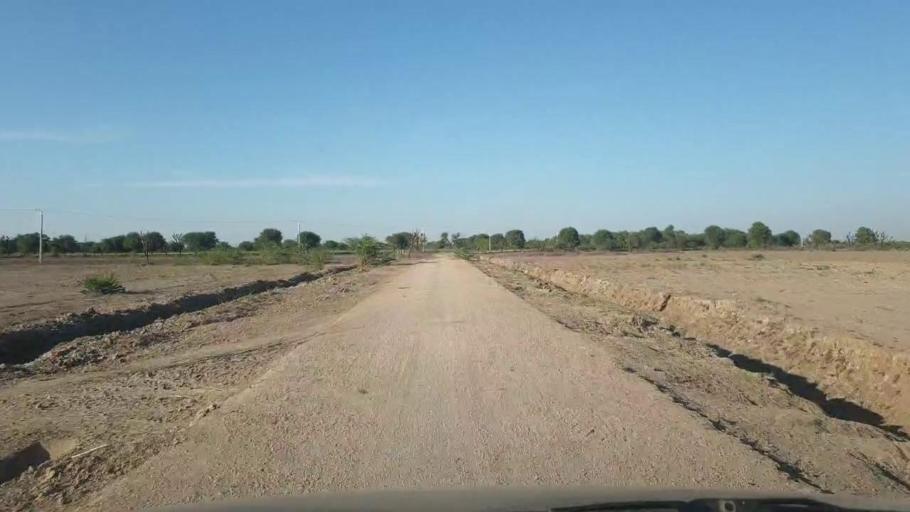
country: PK
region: Sindh
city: Dhoro Naro
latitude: 25.4351
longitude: 69.5364
